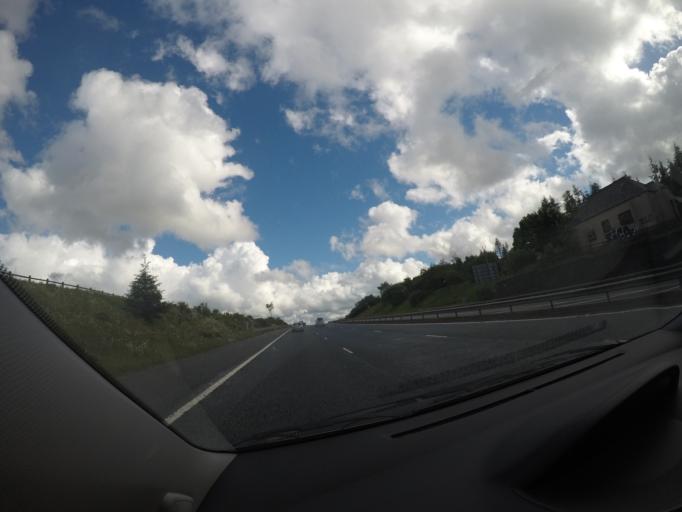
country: GB
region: Scotland
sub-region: South Lanarkshire
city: Douglas
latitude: 55.5662
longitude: -3.8064
